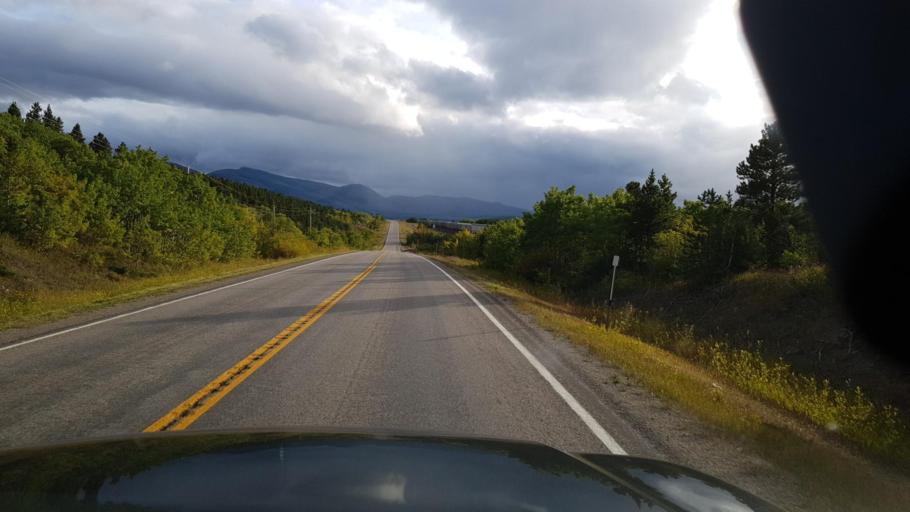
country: US
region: Montana
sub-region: Glacier County
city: South Browning
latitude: 48.3805
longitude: -113.2743
